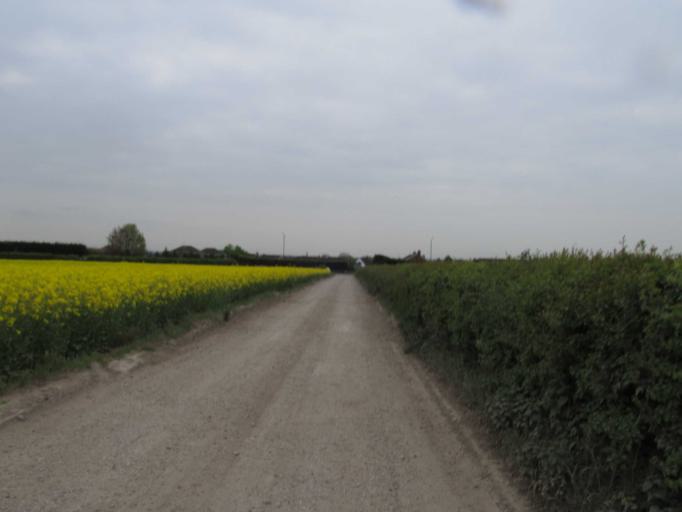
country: GB
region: England
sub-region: Royal Borough of Windsor and Maidenhead
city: Maidenhead
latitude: 51.5361
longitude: -0.7490
